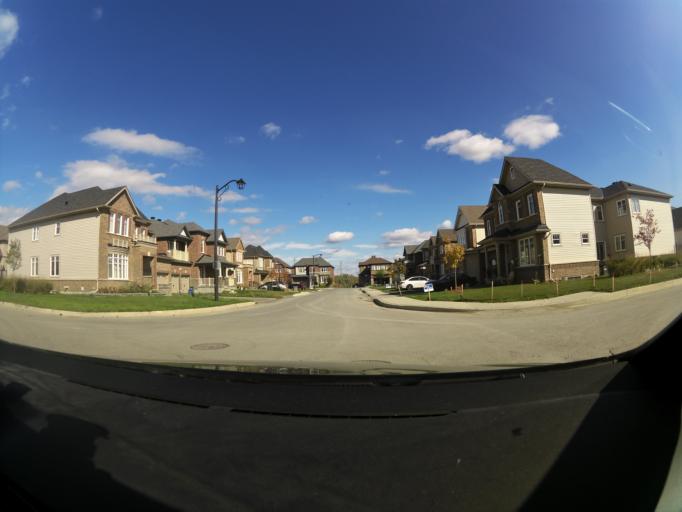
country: CA
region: Ontario
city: Bells Corners
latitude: 45.2776
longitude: -75.8810
